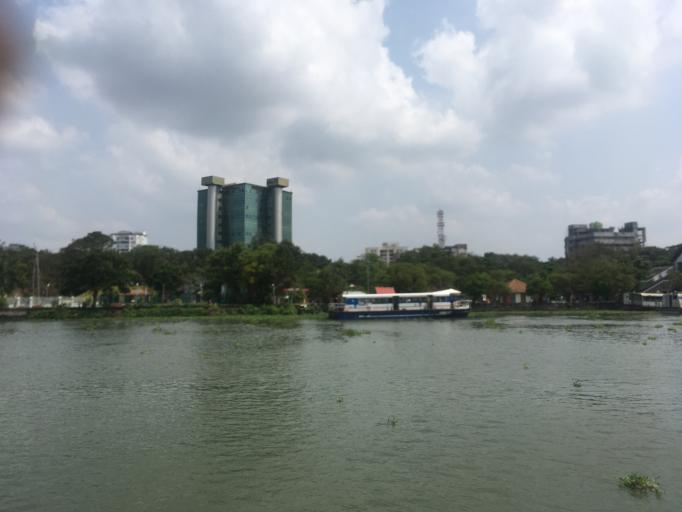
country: IN
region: Kerala
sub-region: Ernakulam
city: Cochin
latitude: 9.9731
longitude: 76.2772
